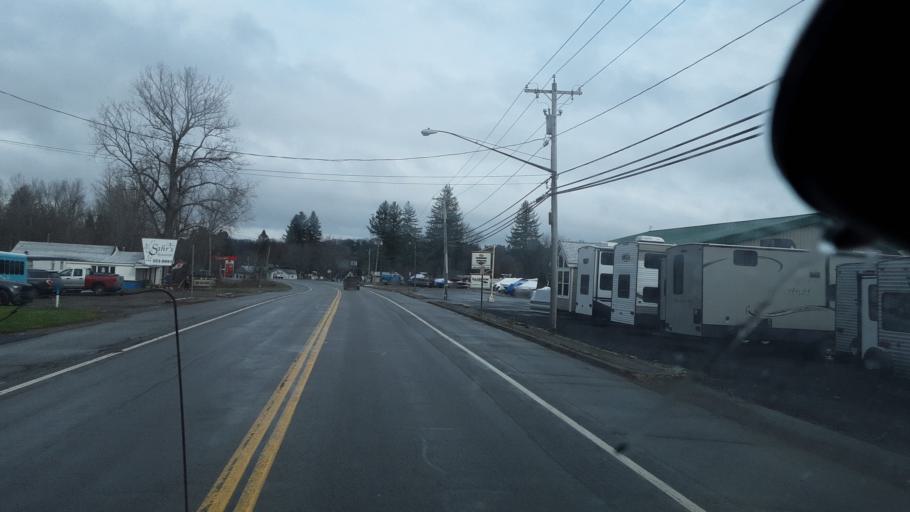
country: US
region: New York
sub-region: Cattaraugus County
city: Delevan
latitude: 42.4320
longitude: -78.4814
